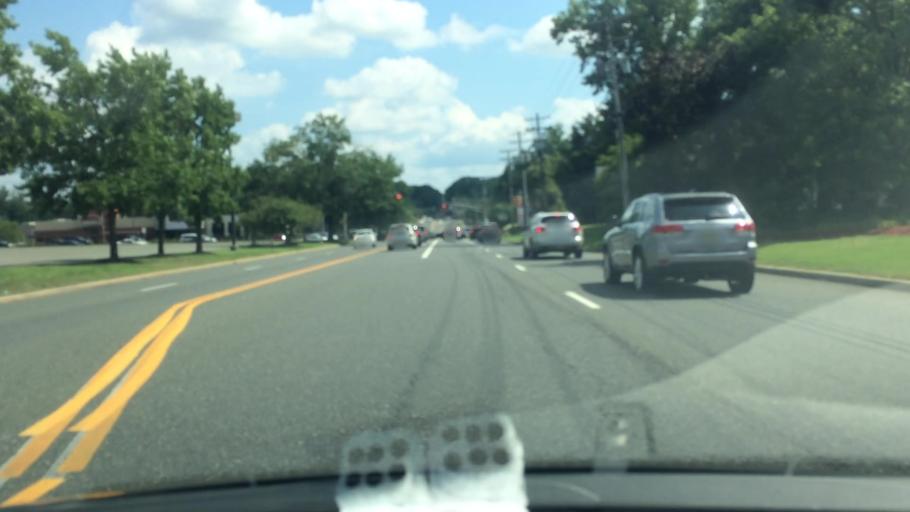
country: US
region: New Jersey
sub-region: Camden County
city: Glendora
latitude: 39.8295
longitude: -75.1006
